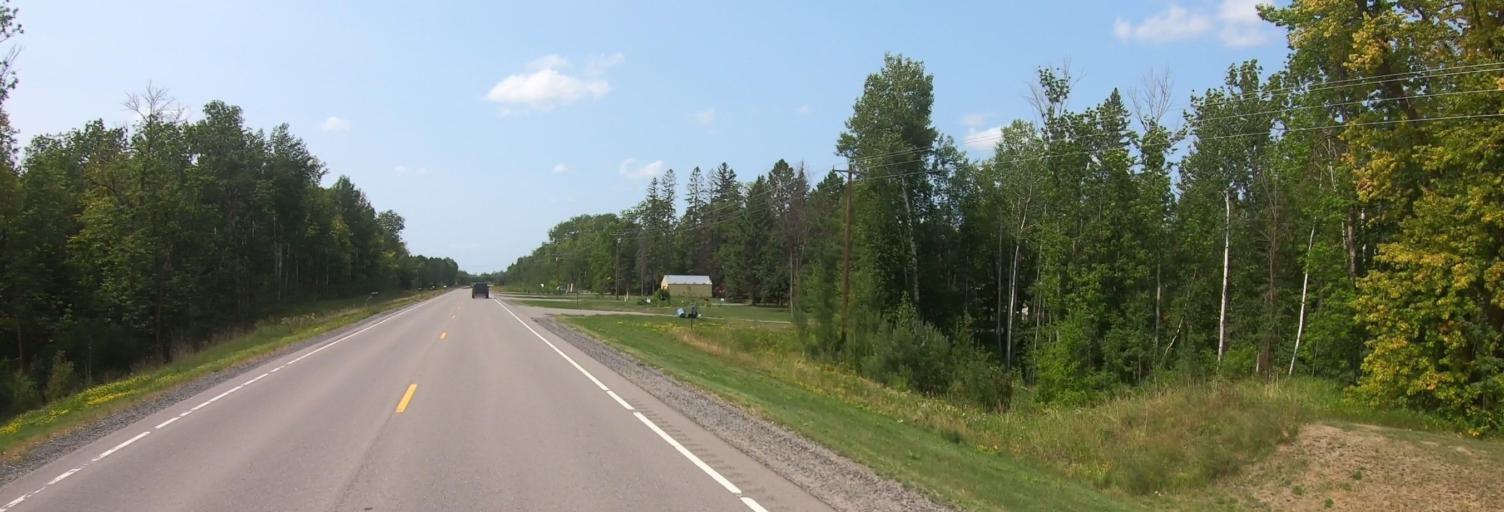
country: US
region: Minnesota
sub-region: Lake of the Woods County
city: Baudette
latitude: 48.6986
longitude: -94.5293
